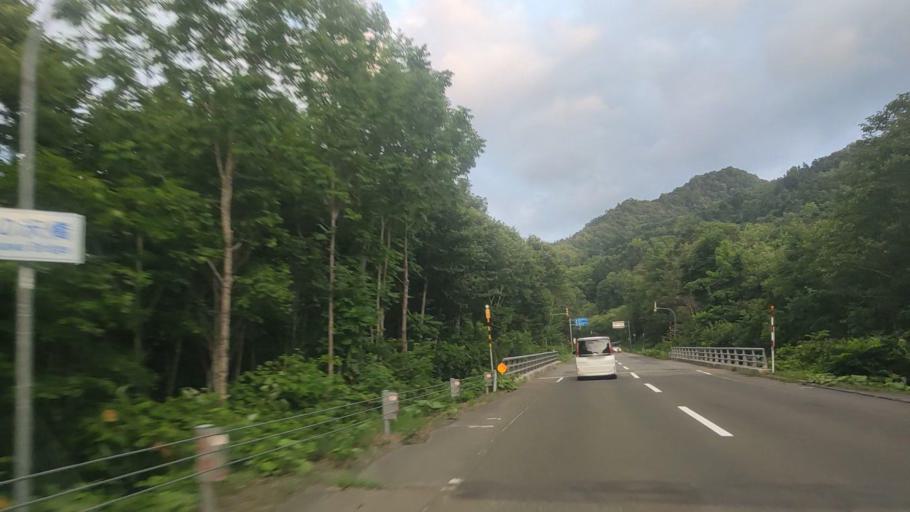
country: JP
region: Hokkaido
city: Ashibetsu
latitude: 43.3679
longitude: 142.2283
